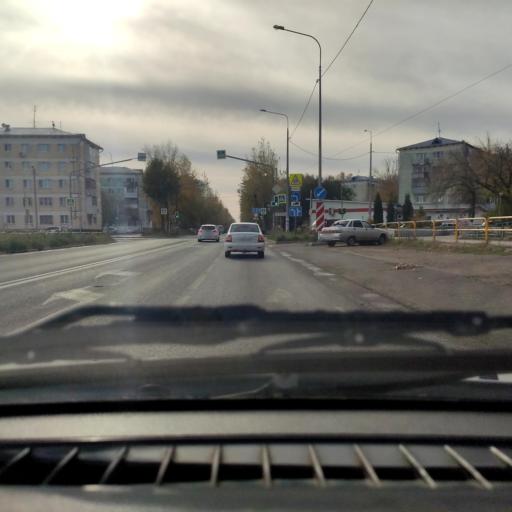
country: RU
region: Samara
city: Tol'yatti
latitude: 53.5382
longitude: 49.4096
